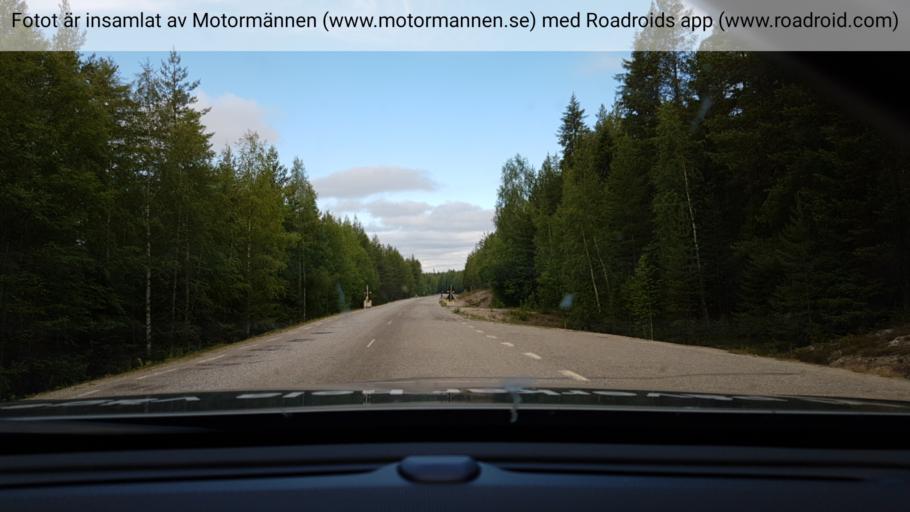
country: SE
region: Vaesterbotten
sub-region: Norsjo Kommun
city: Norsjoe
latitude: 64.6868
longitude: 19.2202
